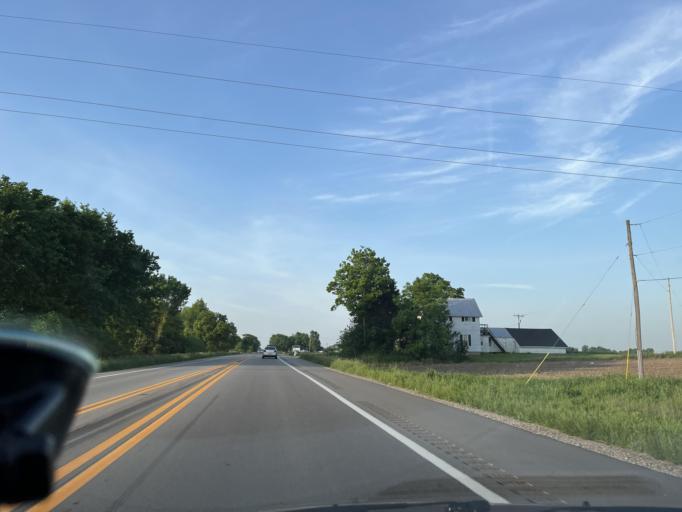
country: US
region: Michigan
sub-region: Kent County
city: Caledonia
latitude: 42.7760
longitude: -85.5067
